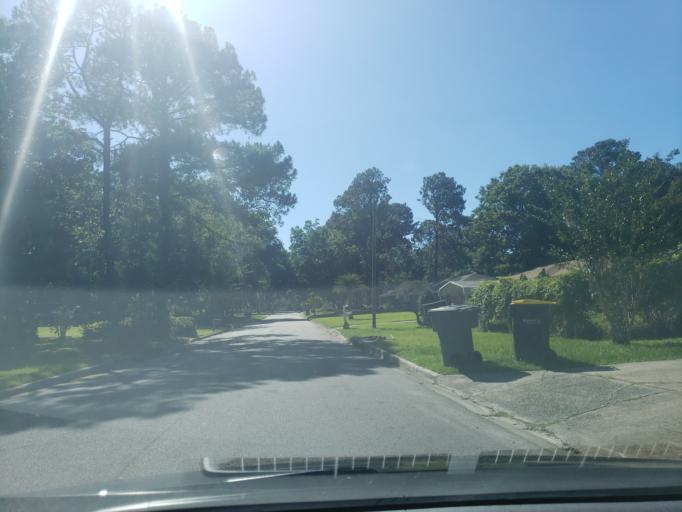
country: US
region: Georgia
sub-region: Chatham County
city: Montgomery
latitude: 31.9910
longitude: -81.1428
